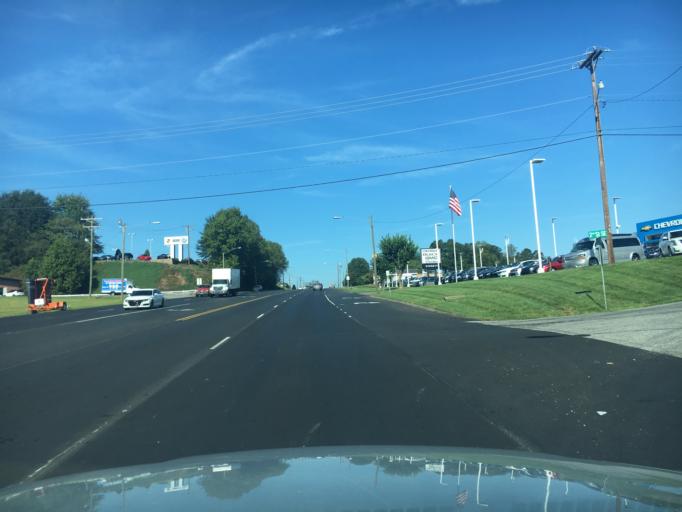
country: US
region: North Carolina
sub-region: Catawba County
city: Hickory
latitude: 35.7134
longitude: -81.3326
